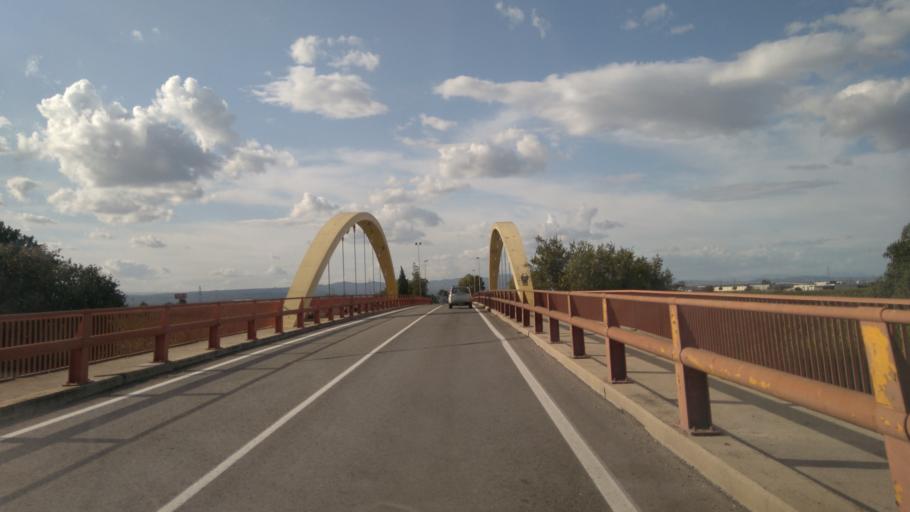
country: ES
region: Valencia
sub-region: Provincia de Valencia
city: Alzira
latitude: 39.1624
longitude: -0.4354
